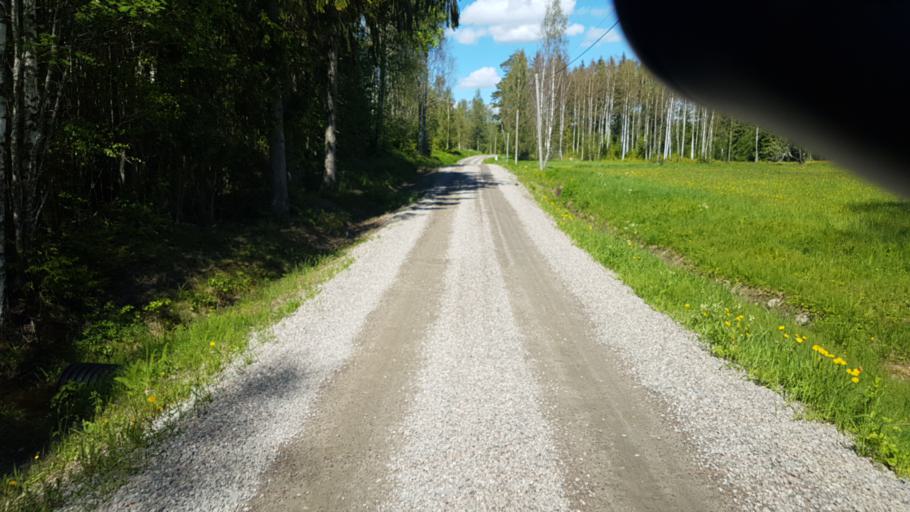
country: SE
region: Vaermland
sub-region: Arvika Kommun
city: Arvika
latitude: 59.5723
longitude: 12.8328
